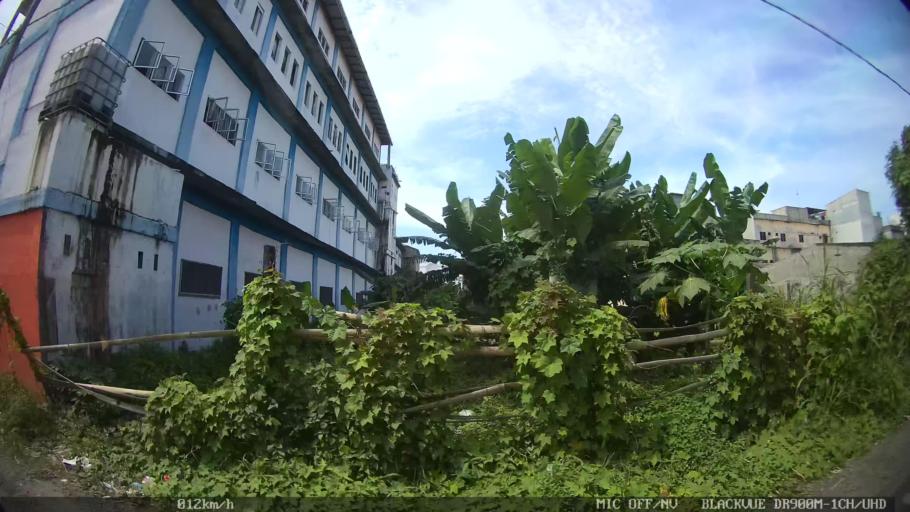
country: ID
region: North Sumatra
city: Labuhan Deli
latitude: 3.6886
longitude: 98.6587
